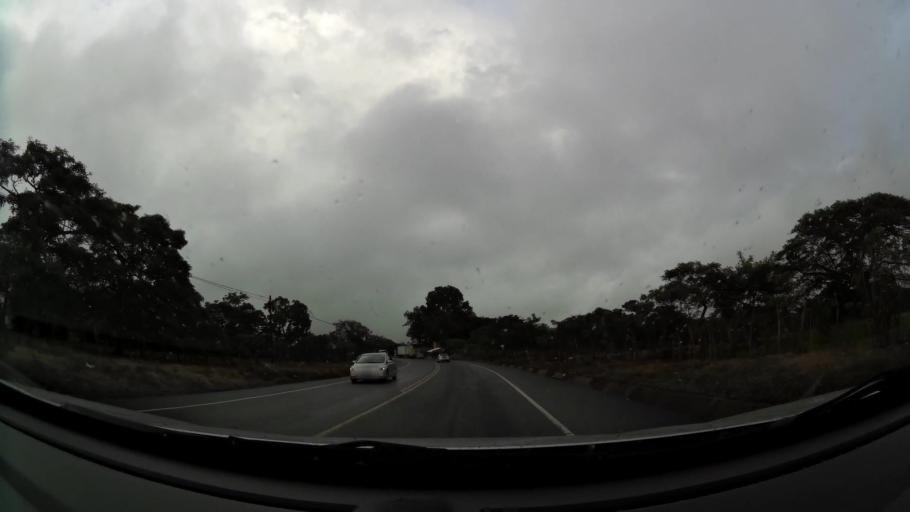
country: CR
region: Alajuela
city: Carrillos
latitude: 9.9788
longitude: -84.2704
